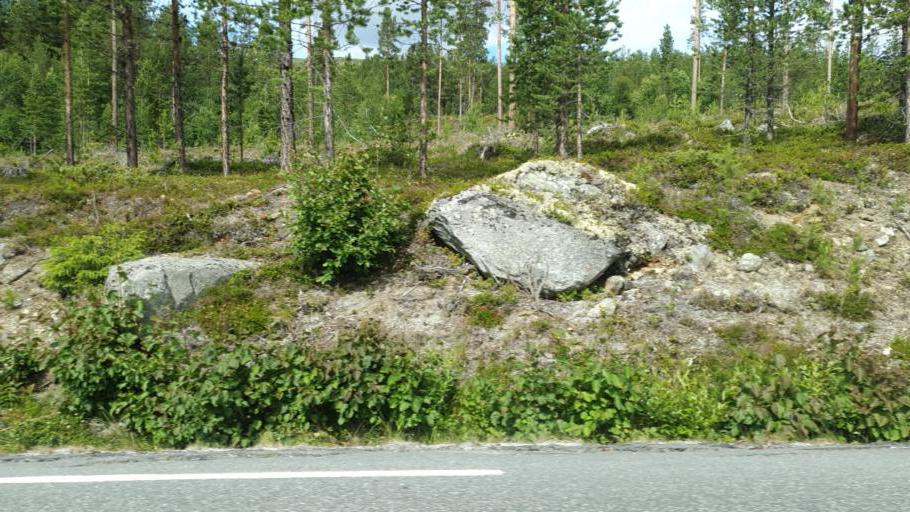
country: NO
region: Oppland
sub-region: Vaga
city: Vagamo
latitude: 61.7334
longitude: 9.0883
